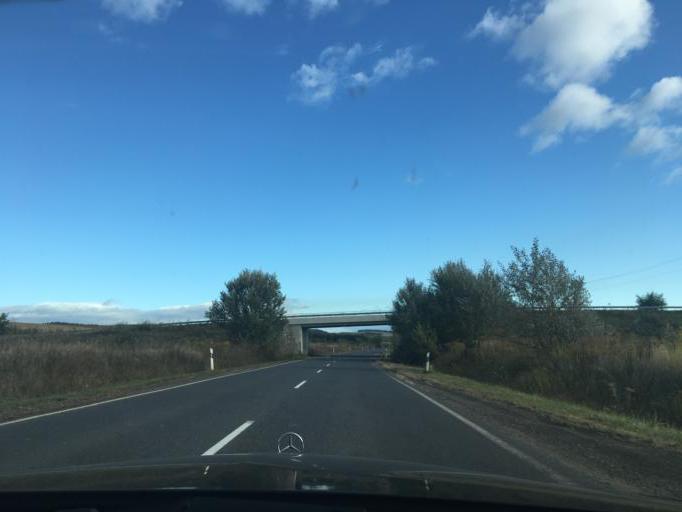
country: HU
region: Borsod-Abauj-Zemplen
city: Gonc
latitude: 48.5021
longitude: 21.2215
